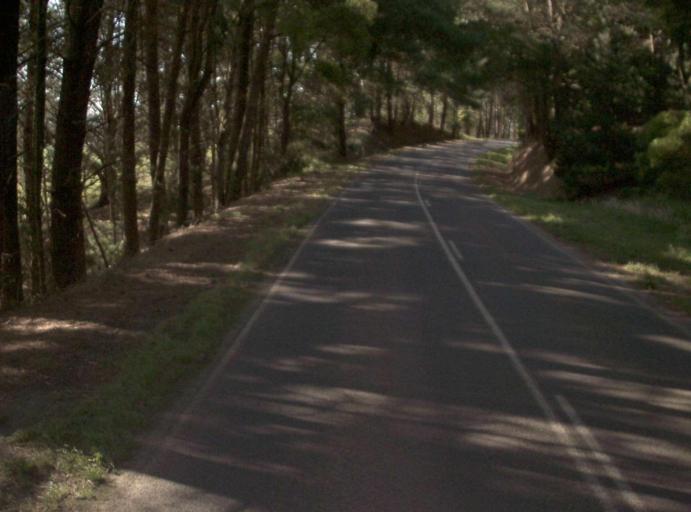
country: AU
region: Victoria
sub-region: Latrobe
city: Moe
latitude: -38.4670
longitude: 146.1364
